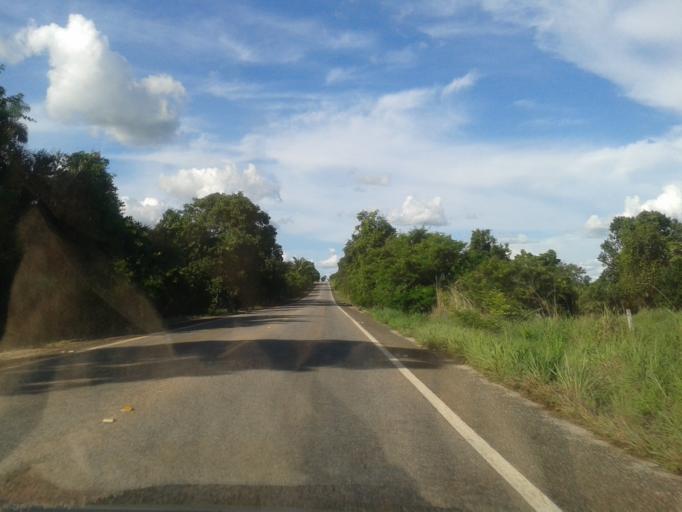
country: BR
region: Goias
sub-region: Mozarlandia
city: Mozarlandia
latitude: -14.5403
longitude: -50.4895
